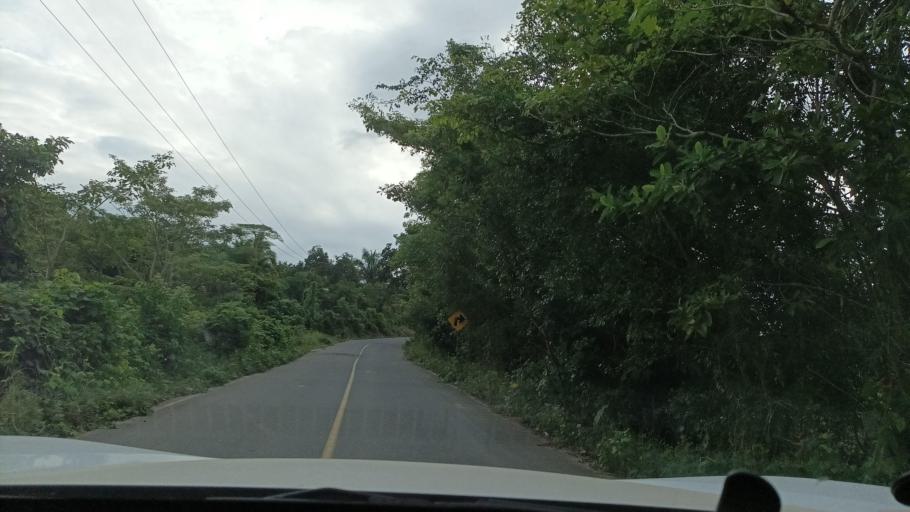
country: MX
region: Veracruz
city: Hidalgotitlan
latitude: 17.7190
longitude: -94.4797
